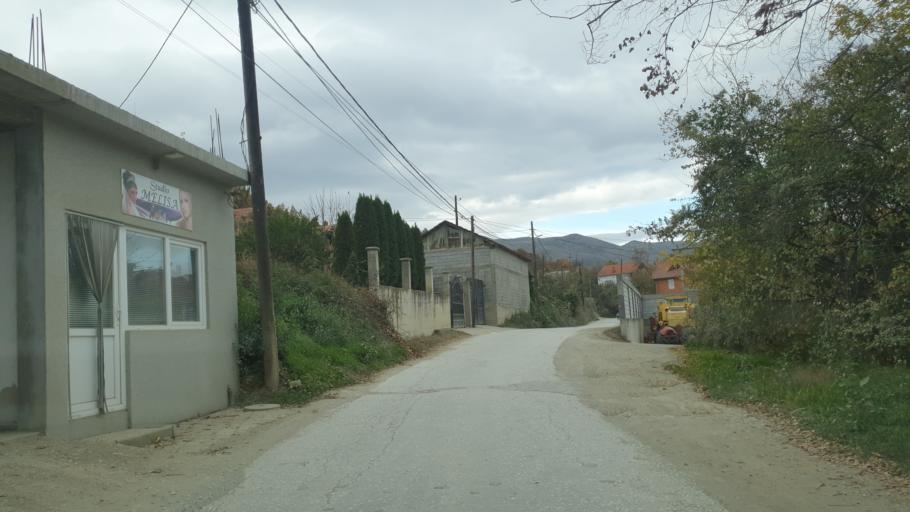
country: MK
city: Kondovo
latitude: 42.0327
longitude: 21.2833
